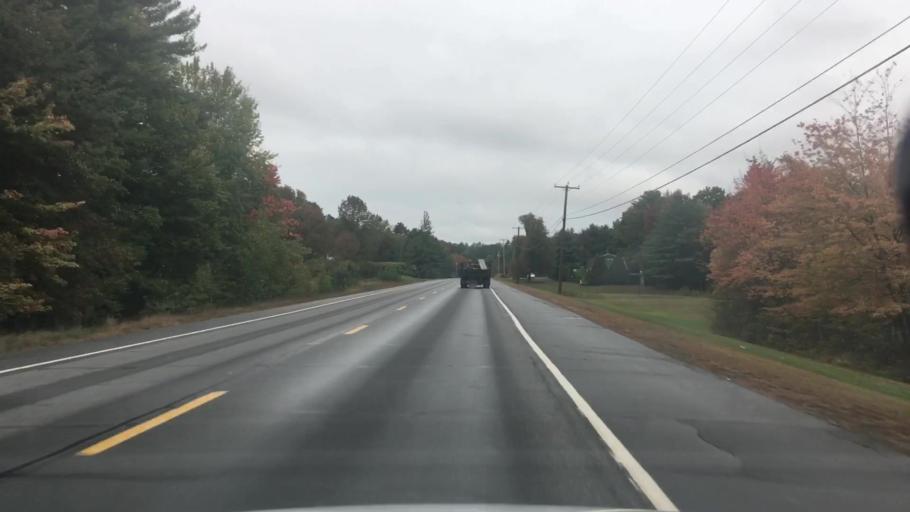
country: US
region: Maine
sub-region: Kennebec County
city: Belgrade
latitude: 44.4299
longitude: -69.8317
